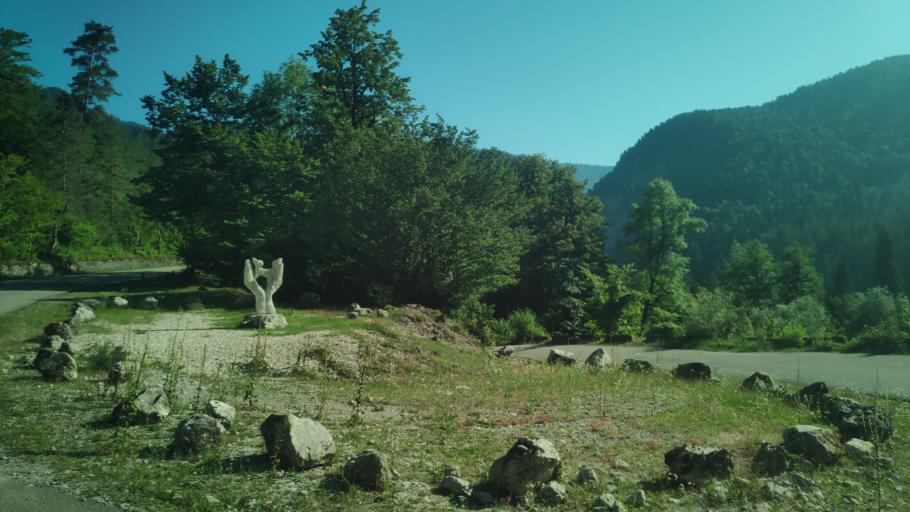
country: GE
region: Abkhazia
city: Gagra
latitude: 43.4536
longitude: 40.5453
